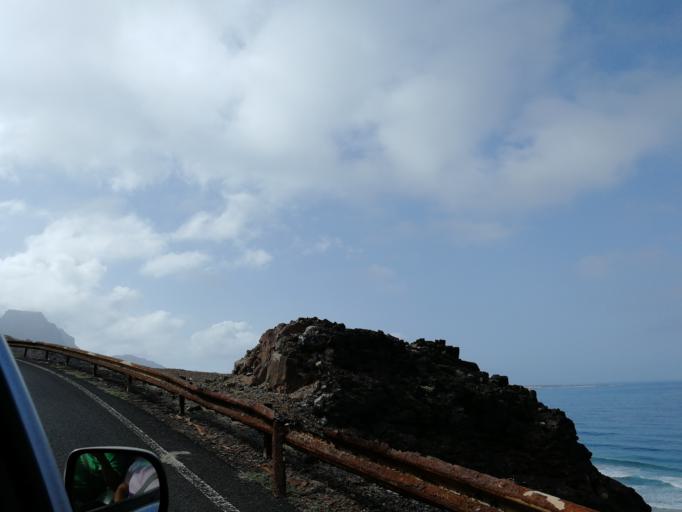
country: CV
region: Sao Vicente
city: Mindelo
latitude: 16.8660
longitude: -24.8963
